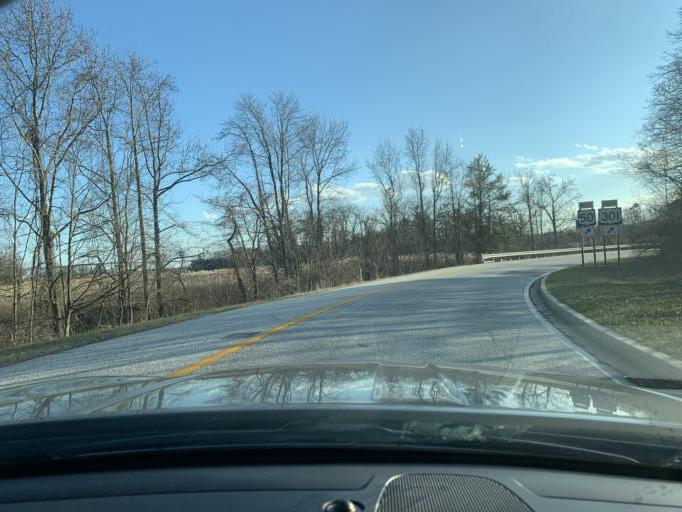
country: US
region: Maryland
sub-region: Anne Arundel County
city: Cape Saint Claire
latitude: 39.0177
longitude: -76.4075
